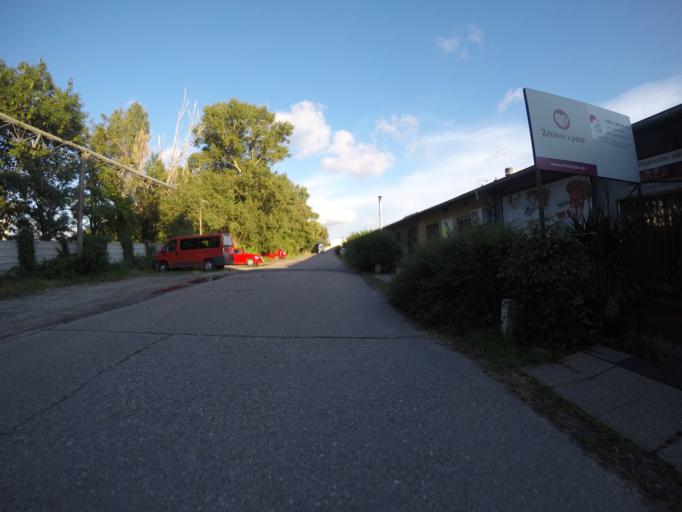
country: SK
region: Bratislavsky
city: Bratislava
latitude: 48.1721
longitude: 17.1536
